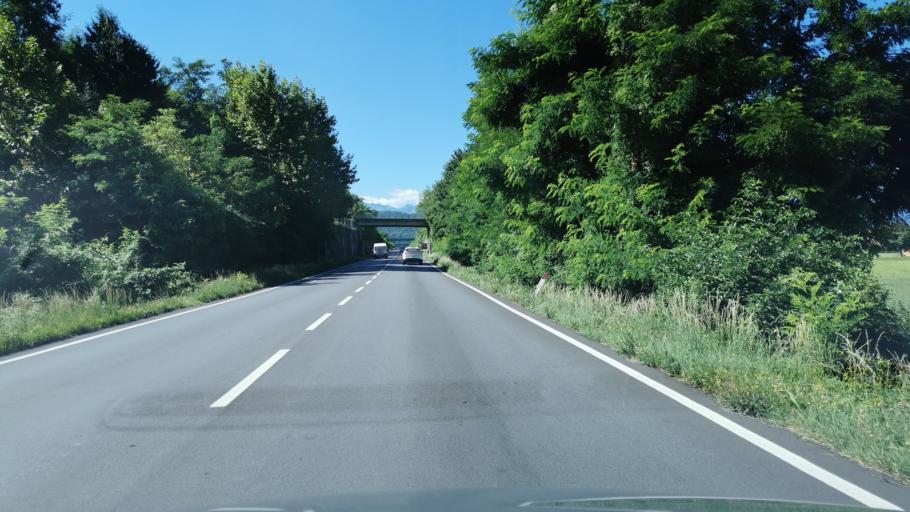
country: IT
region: Piedmont
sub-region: Provincia di Cuneo
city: Boves
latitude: 44.3584
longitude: 7.5490
